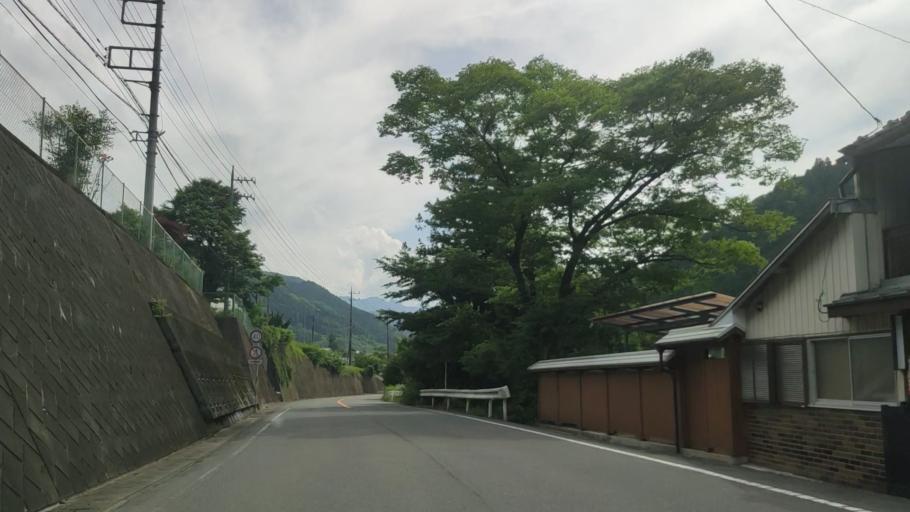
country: JP
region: Gunma
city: Tomioka
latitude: 36.1855
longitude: 138.7479
